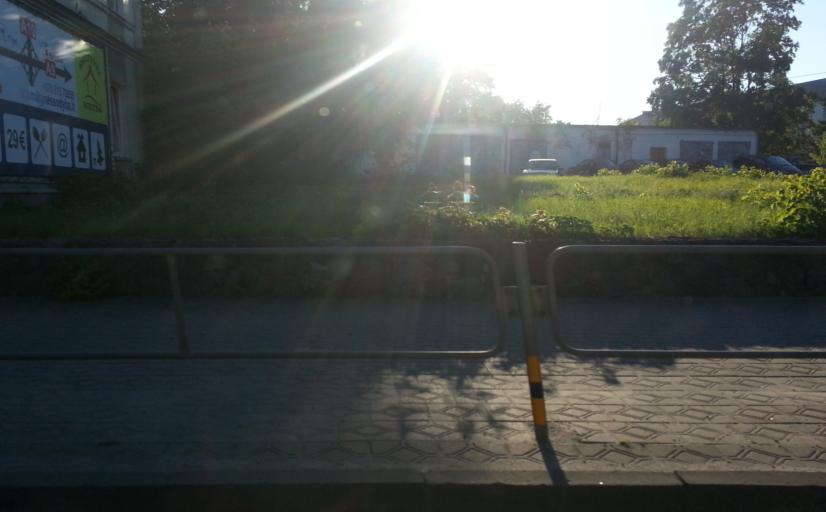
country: LT
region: Panevezys
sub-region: Panevezys City
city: Panevezys
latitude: 55.7333
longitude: 24.3683
